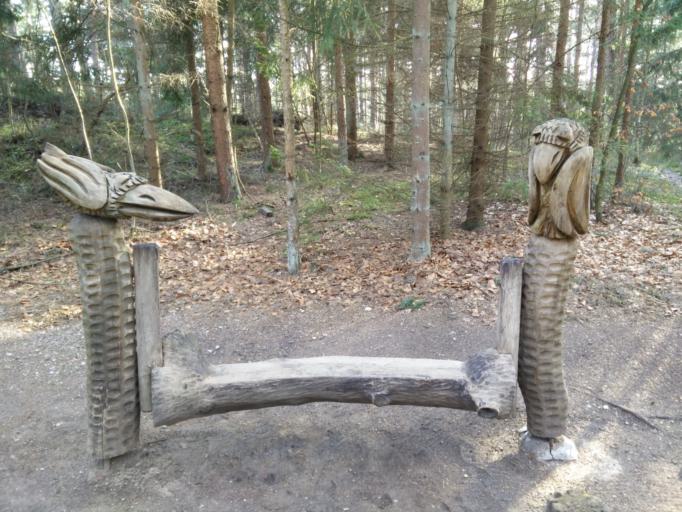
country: LT
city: Neringa
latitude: 55.5357
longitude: 21.1113
